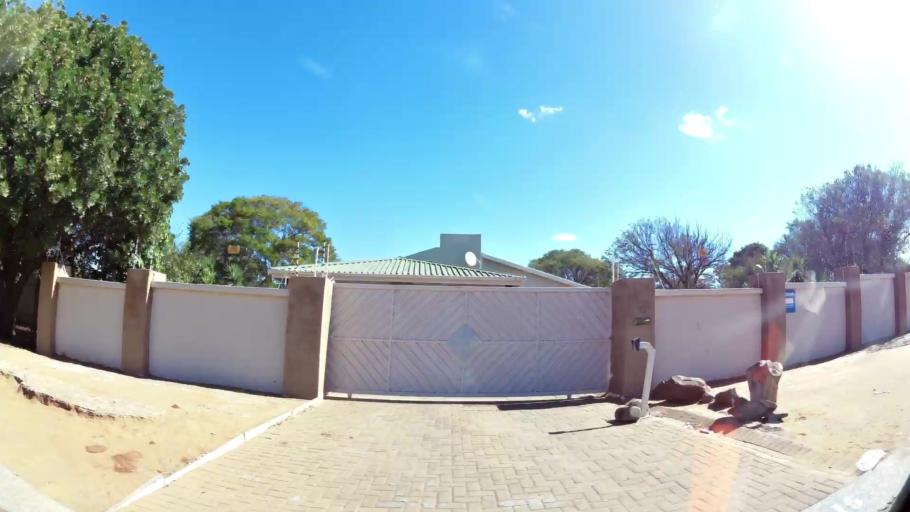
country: ZA
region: Limpopo
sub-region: Capricorn District Municipality
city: Polokwane
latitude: -23.9112
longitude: 29.4790
